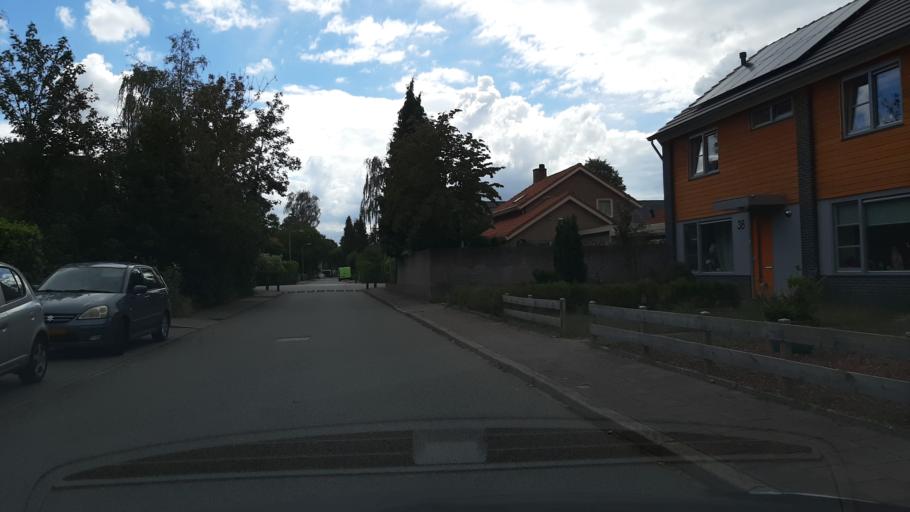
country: NL
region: Gelderland
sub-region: Gemeente Ermelo
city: Ermelo
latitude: 52.2959
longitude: 5.6272
